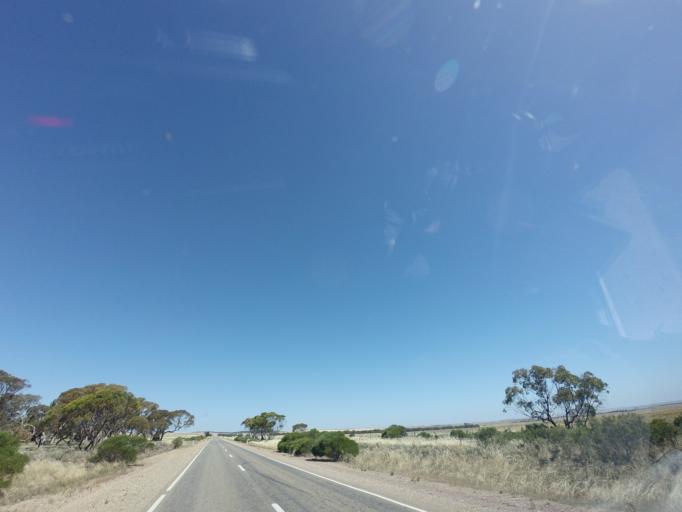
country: AU
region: South Australia
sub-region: Peterborough
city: Peterborough
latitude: -32.9591
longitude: 138.7974
